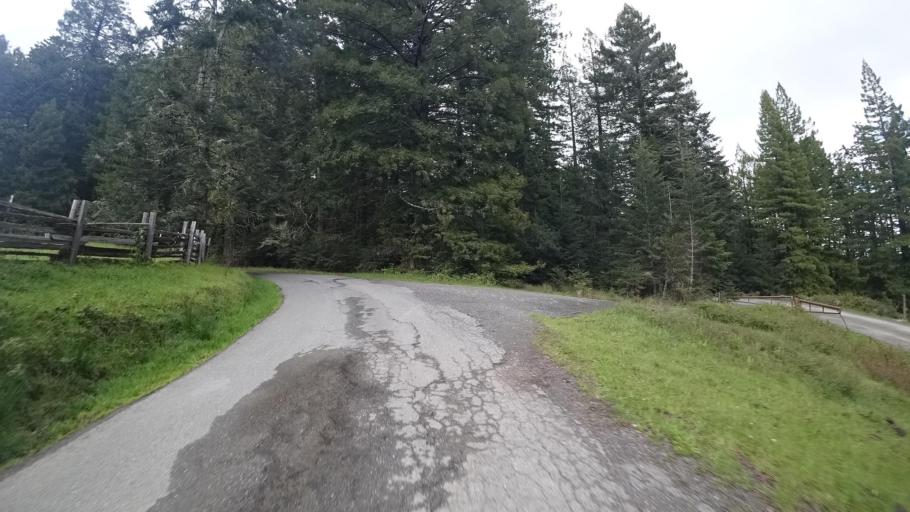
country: US
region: California
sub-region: Humboldt County
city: Blue Lake
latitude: 40.9085
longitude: -123.9660
